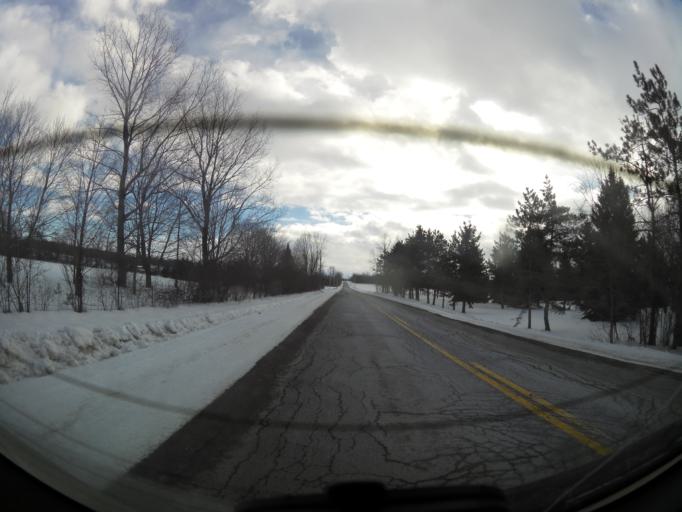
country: CA
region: Ontario
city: Ottawa
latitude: 45.2563
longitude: -75.4568
